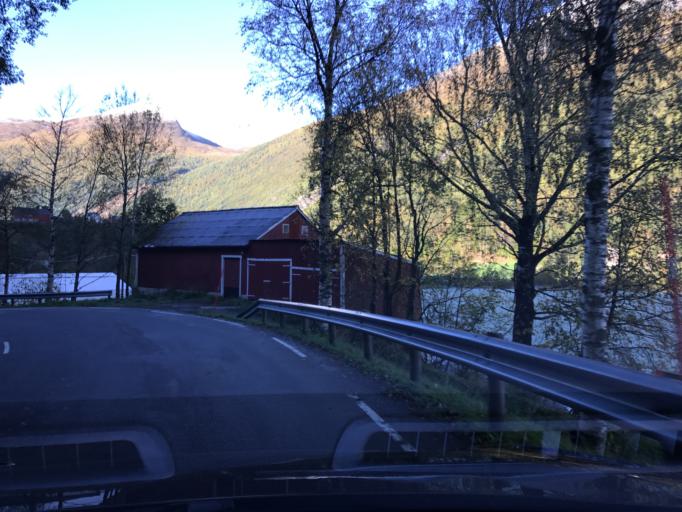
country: NO
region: More og Romsdal
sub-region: Norddal
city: Valldal
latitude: 62.3147
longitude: 7.2948
